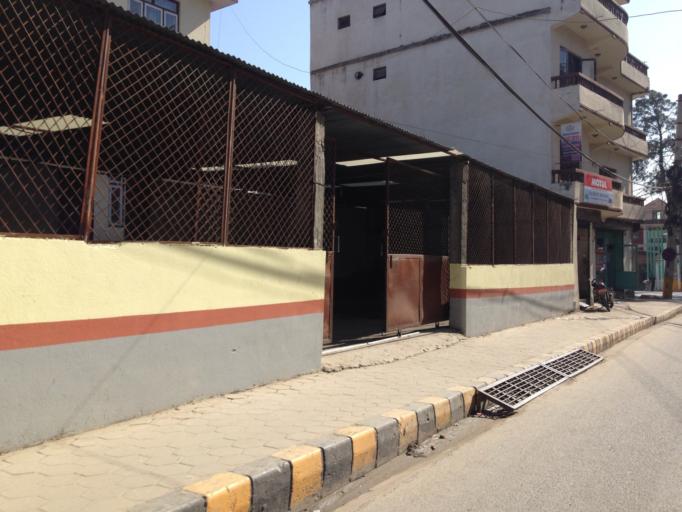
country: NP
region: Central Region
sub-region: Bagmati Zone
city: Kathmandu
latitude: 27.7268
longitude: 85.3305
